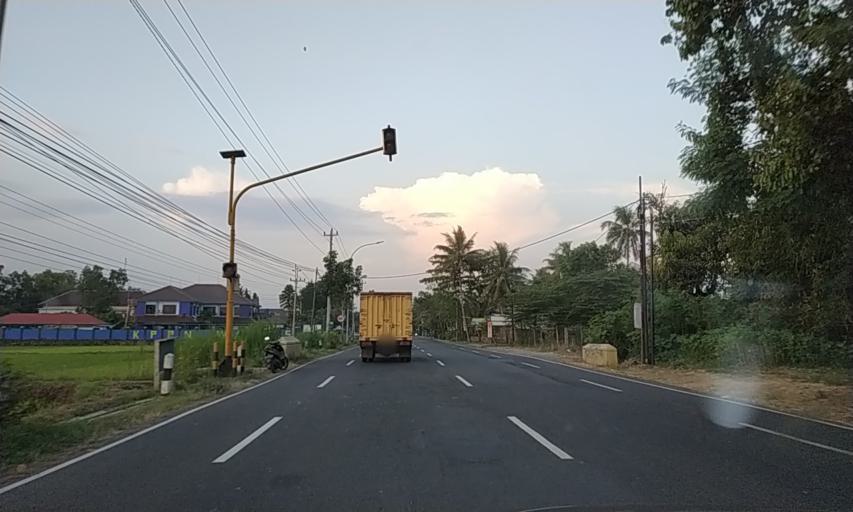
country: ID
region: Daerah Istimewa Yogyakarta
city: Srandakan
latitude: -7.8733
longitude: 110.1379
